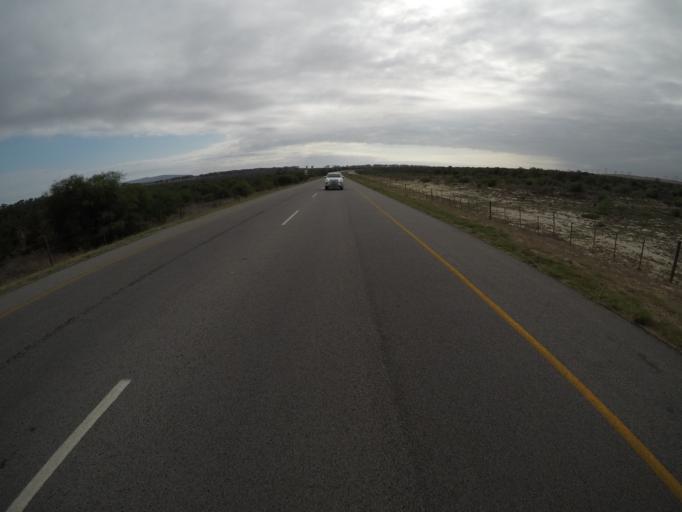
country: ZA
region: Western Cape
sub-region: City of Cape Town
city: Sunset Beach
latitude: -33.7248
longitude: 18.5272
